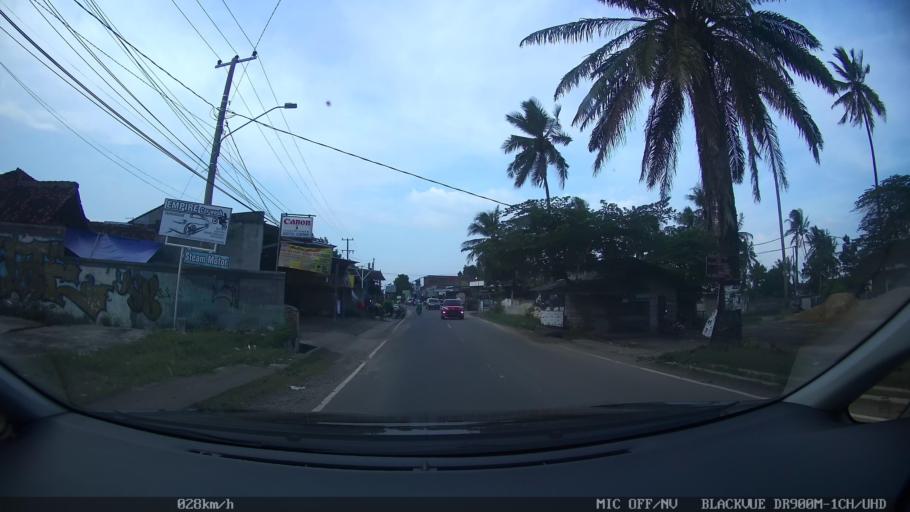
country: ID
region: Lampung
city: Kedaton
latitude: -5.3819
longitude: 105.2340
